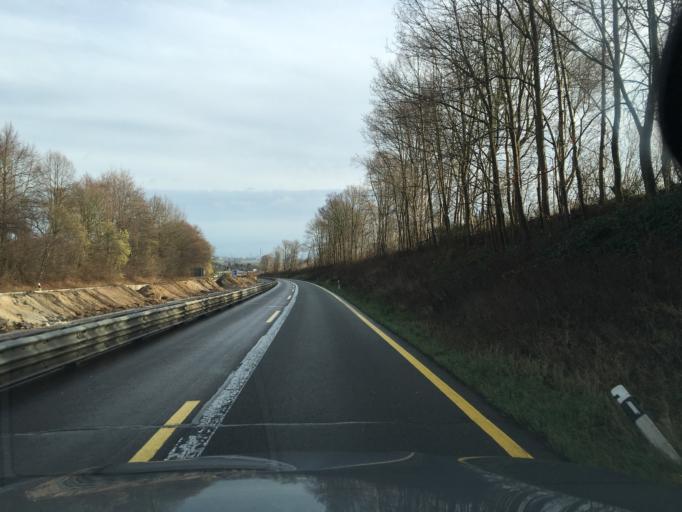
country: DE
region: North Rhine-Westphalia
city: Bruhl
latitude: 50.7982
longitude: 6.8931
